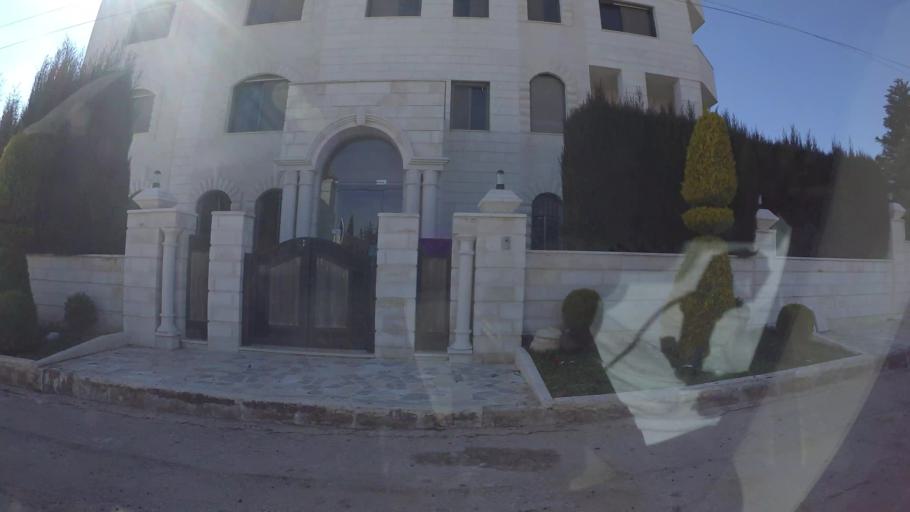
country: JO
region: Amman
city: Al Bunayyat ash Shamaliyah
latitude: 31.9066
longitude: 35.8920
